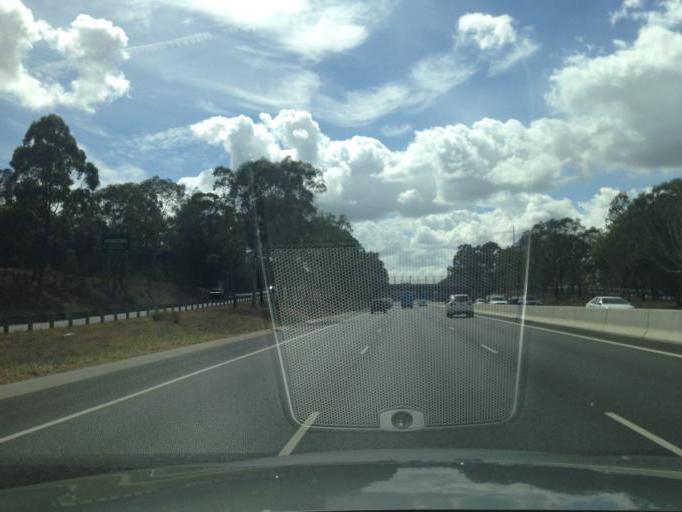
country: AU
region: New South Wales
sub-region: Bankstown
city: Milperra
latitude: -33.9449
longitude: 150.9793
